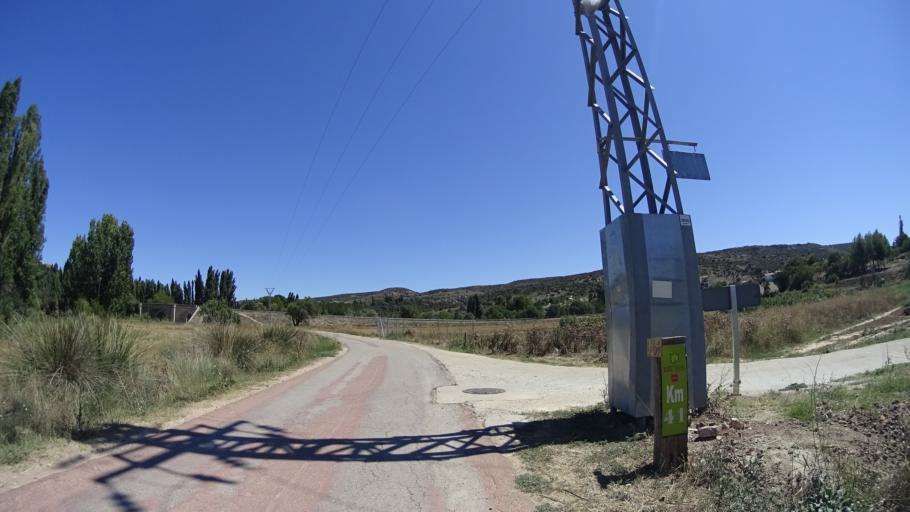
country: ES
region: Madrid
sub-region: Provincia de Madrid
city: Carabana
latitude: 40.2798
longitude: -3.2062
